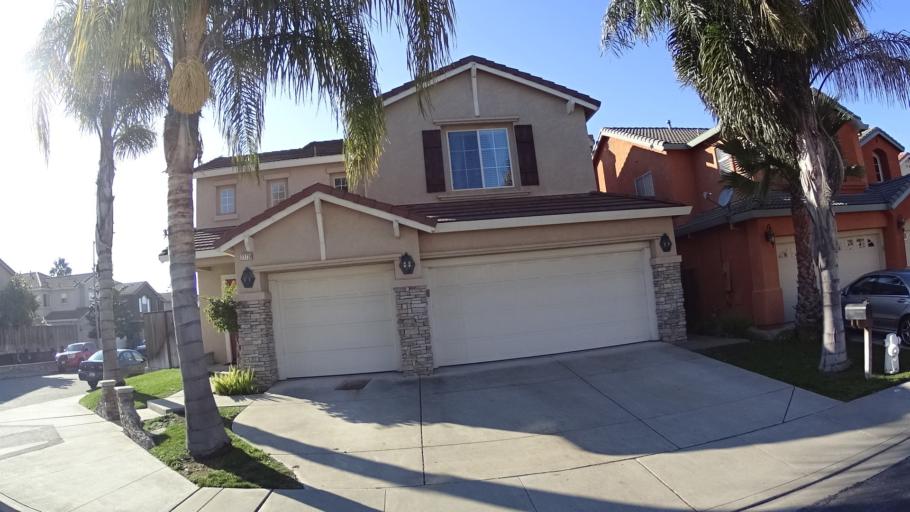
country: US
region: California
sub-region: Alameda County
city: Fairview
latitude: 37.6919
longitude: -122.0412
